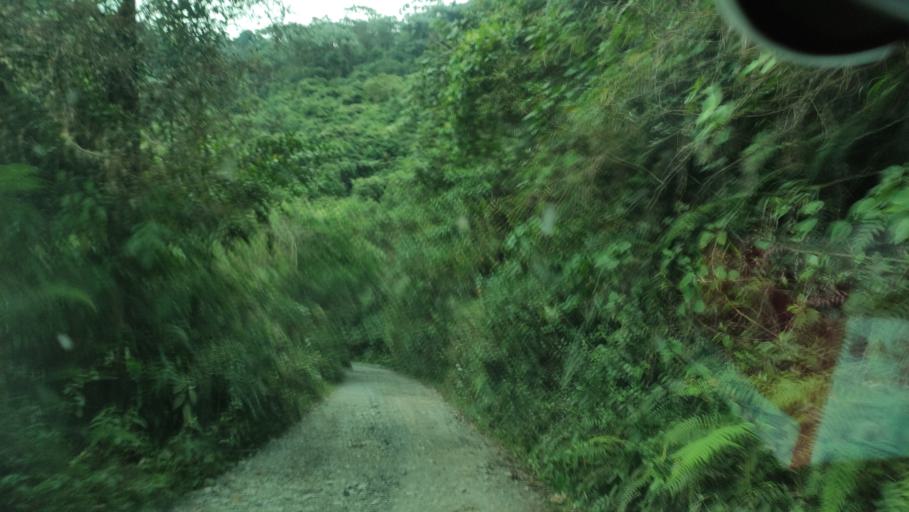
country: CO
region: Valle del Cauca
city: San Pedro
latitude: 3.8800
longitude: -76.1501
